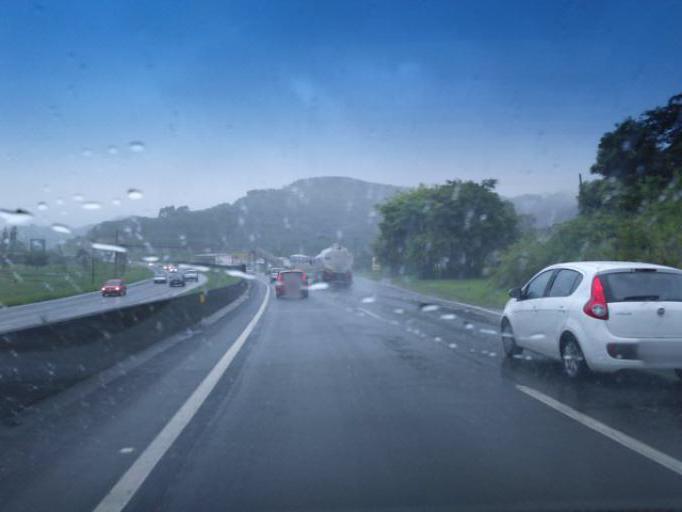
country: BR
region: Santa Catarina
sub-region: Navegantes
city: Navegantes
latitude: -26.8332
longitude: -48.6957
